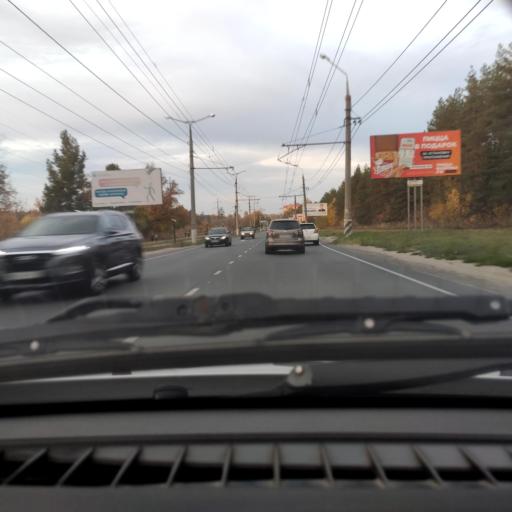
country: RU
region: Samara
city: Tol'yatti
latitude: 53.4944
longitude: 49.3866
